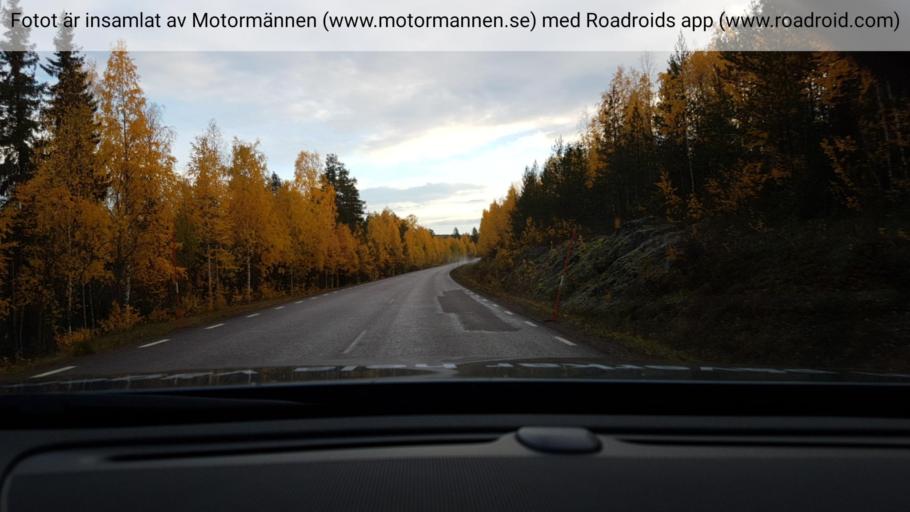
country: SE
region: Norrbotten
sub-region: Overkalix Kommun
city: OEverkalix
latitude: 66.8347
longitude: 22.7556
